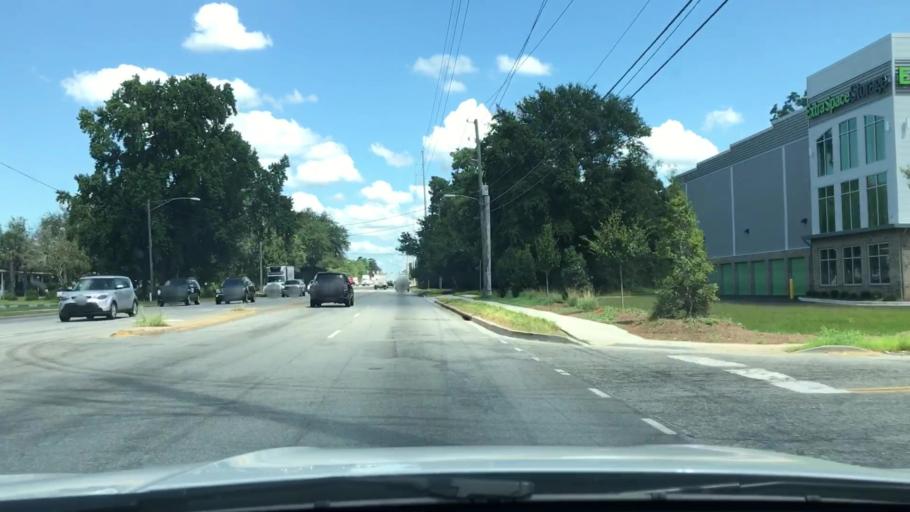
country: US
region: South Carolina
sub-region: Berkeley County
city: Hanahan
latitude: 32.8987
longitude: -79.9855
